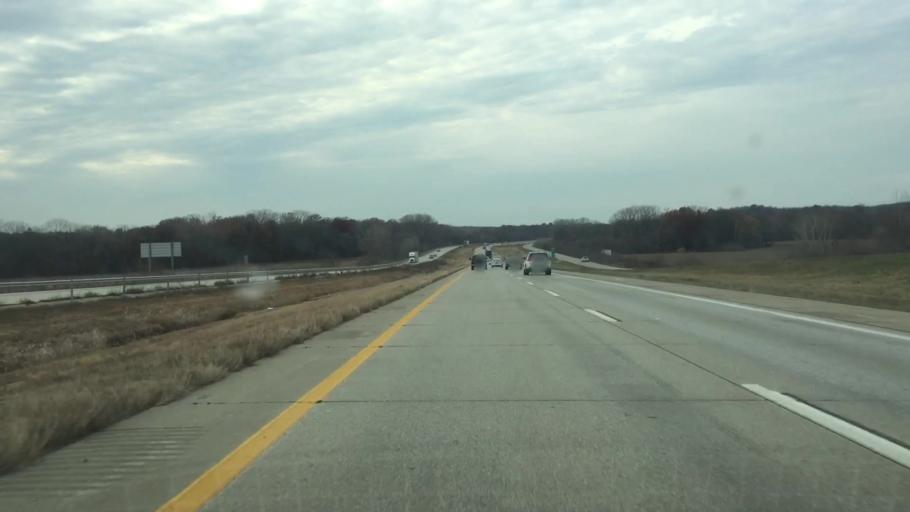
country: US
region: Missouri
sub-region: Cass County
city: Harrisonville
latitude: 38.6635
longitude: -94.3898
